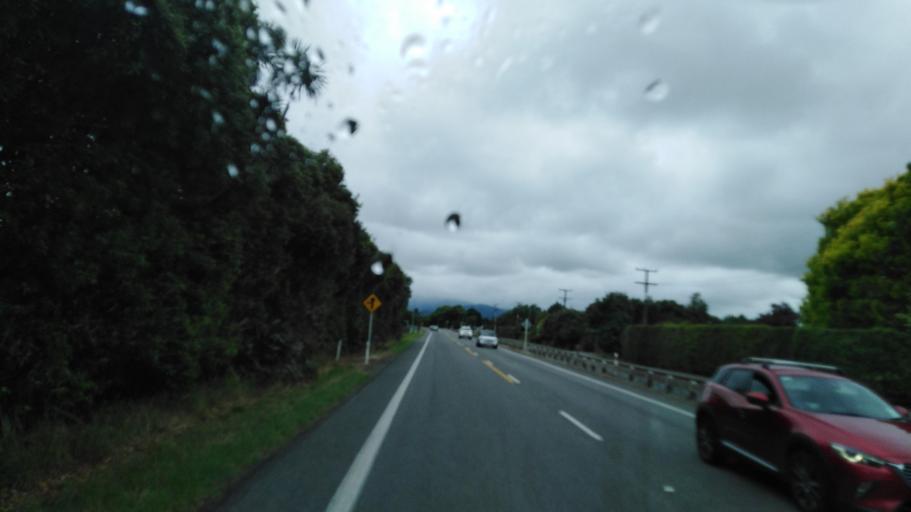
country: NZ
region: Marlborough
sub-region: Marlborough District
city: Blenheim
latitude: -41.4852
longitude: 173.9654
